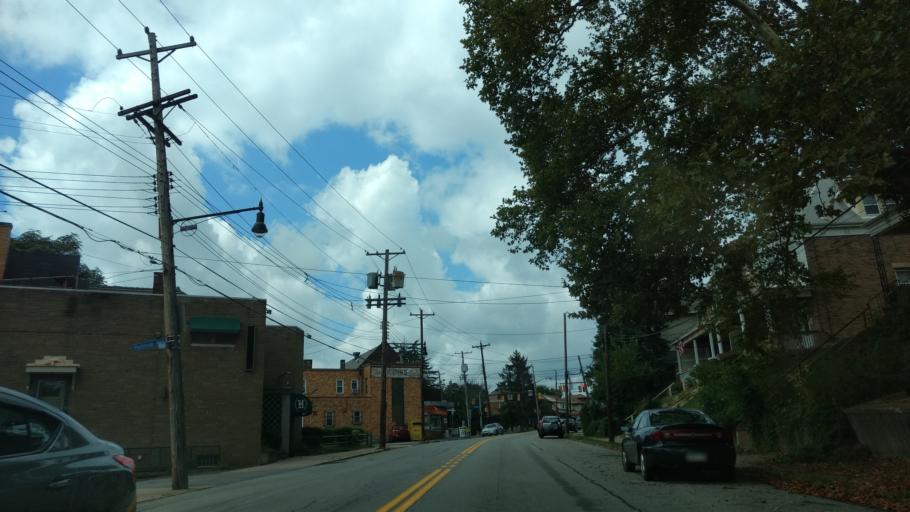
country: US
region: Pennsylvania
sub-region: Allegheny County
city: Bellevue
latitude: 40.4919
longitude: -80.0208
